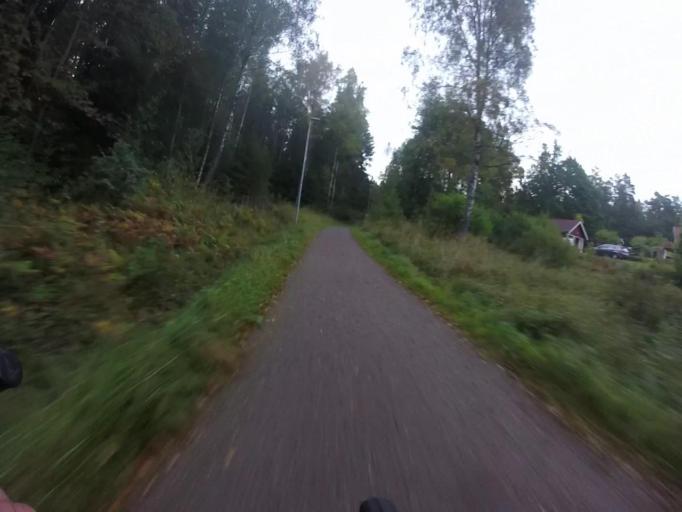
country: SE
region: Vaestra Goetaland
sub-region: Trollhattan
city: Trollhattan
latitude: 58.2908
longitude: 12.2659
